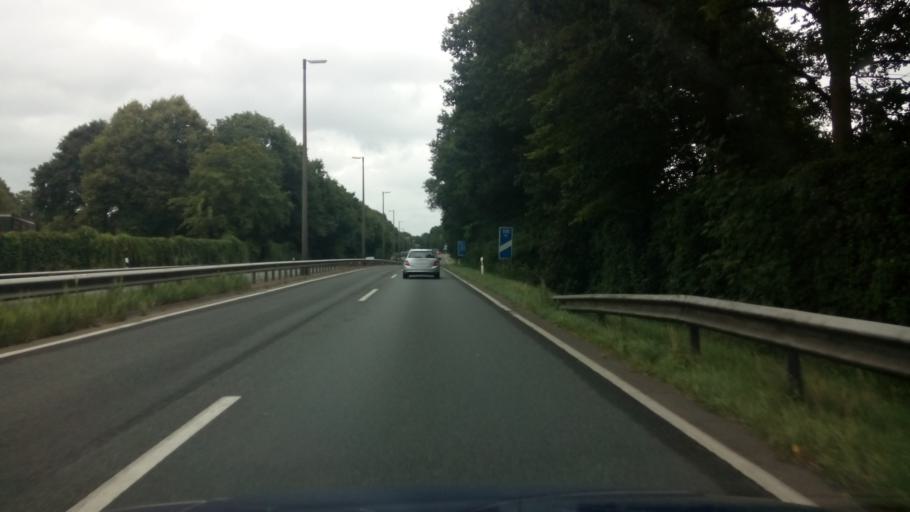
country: DE
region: Lower Saxony
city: Lemwerder
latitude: 53.1808
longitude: 8.6124
